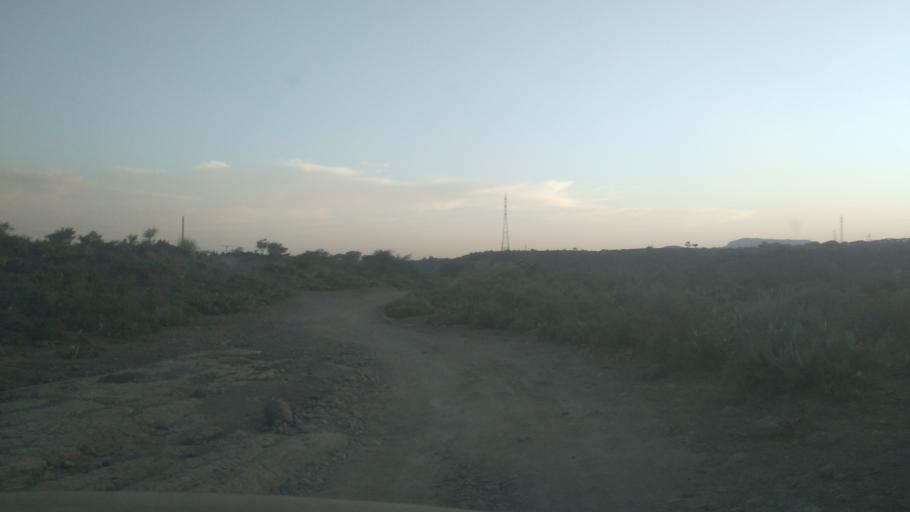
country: ET
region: Oromiya
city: Asbe Teferi
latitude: 9.2421
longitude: 40.7690
